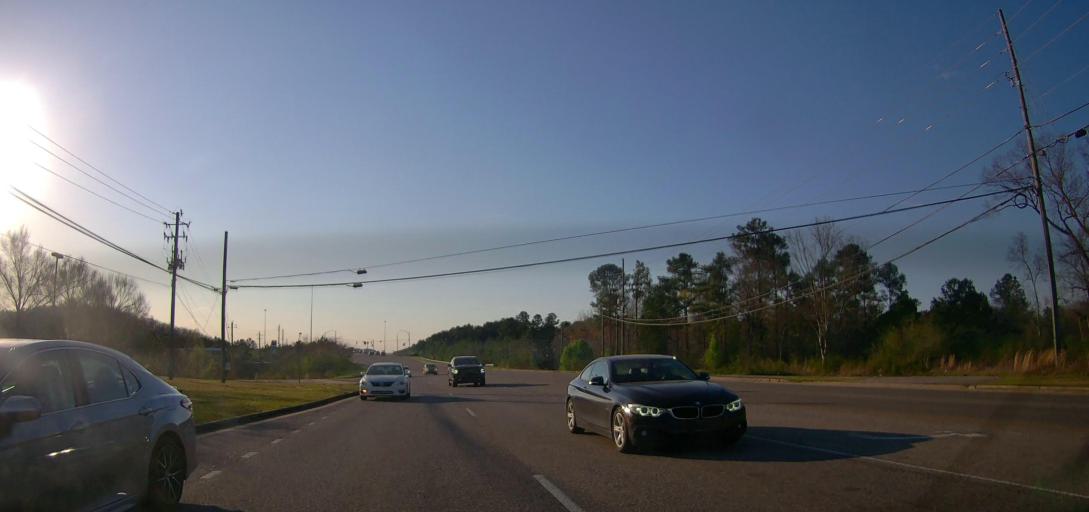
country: US
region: Alabama
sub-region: Shelby County
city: Pelham
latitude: 33.2777
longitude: -86.7945
